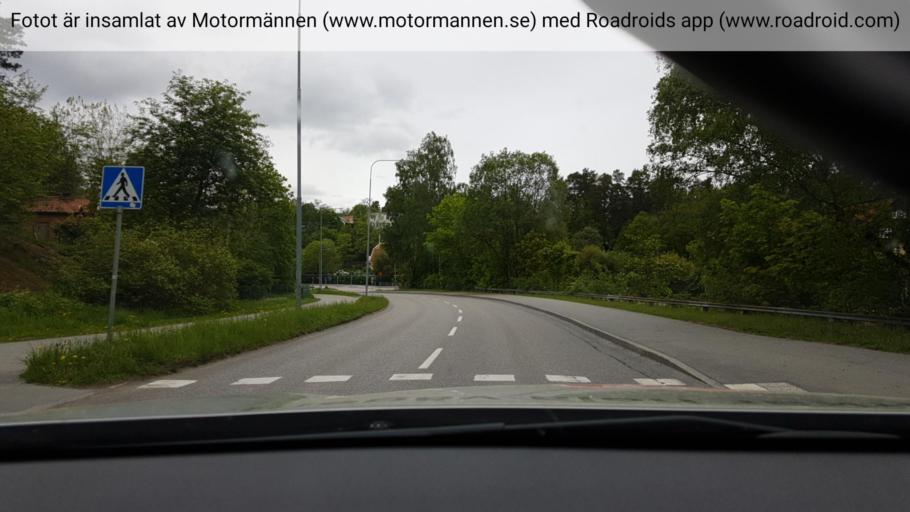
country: SE
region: Stockholm
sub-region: Lidingo
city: Lidingoe
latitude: 59.3700
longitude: 18.1297
